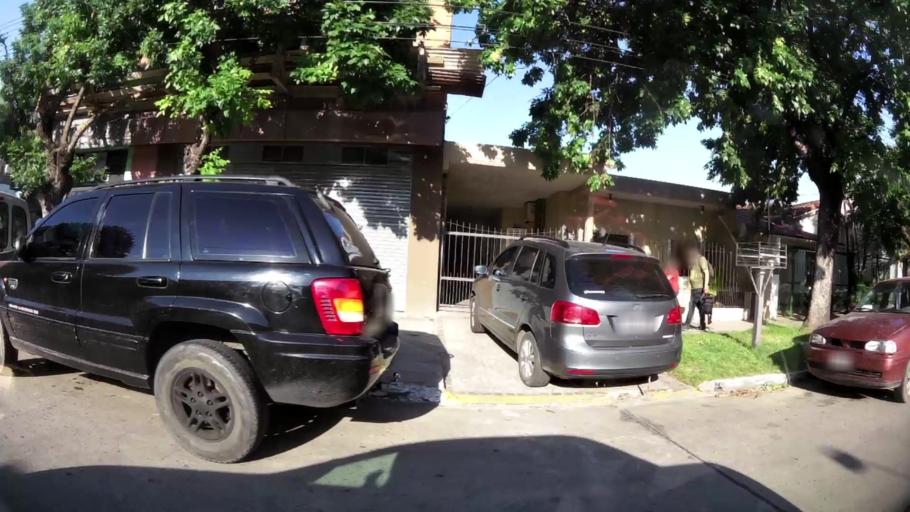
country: AR
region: Buenos Aires
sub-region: Partido de Merlo
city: Merlo
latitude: -34.6713
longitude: -58.7236
